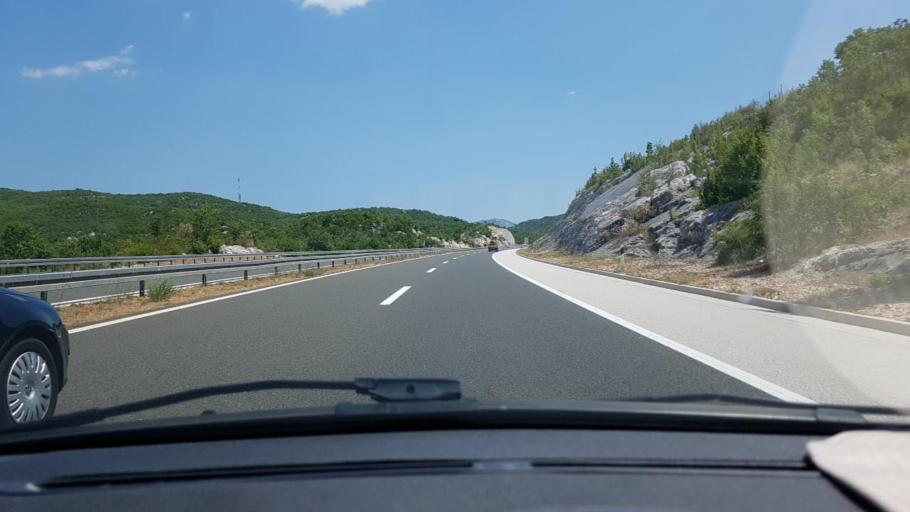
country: HR
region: Splitsko-Dalmatinska
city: Grubine
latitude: 43.3482
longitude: 17.1316
